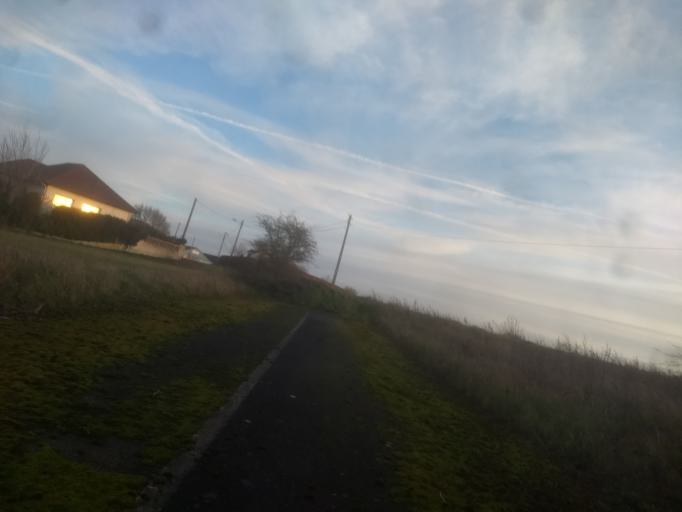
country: FR
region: Nord-Pas-de-Calais
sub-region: Departement du Pas-de-Calais
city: Achicourt
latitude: 50.2765
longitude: 2.7486
